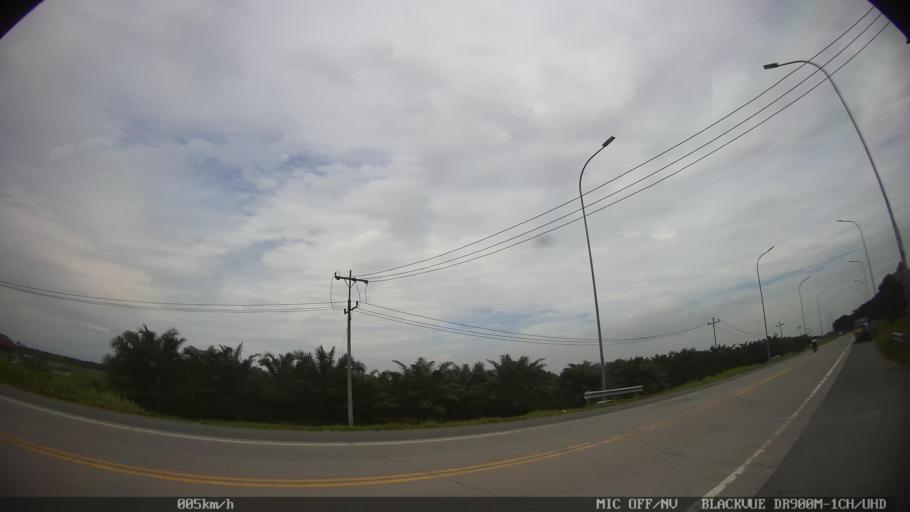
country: ID
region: North Sumatra
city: Sunggal
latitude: 3.6195
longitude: 98.5764
